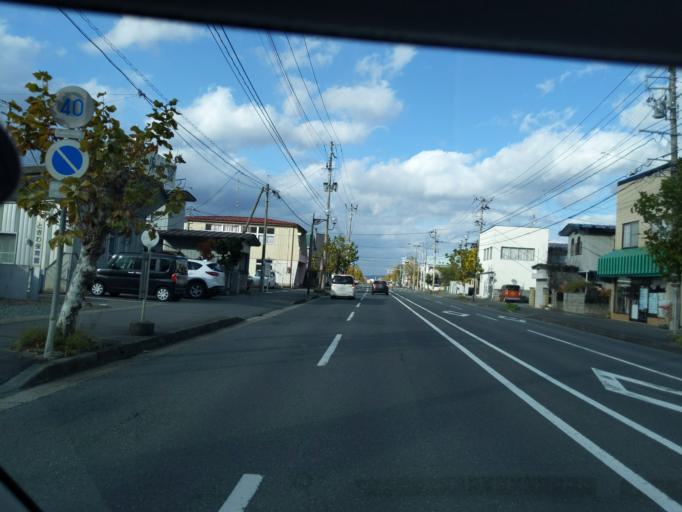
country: JP
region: Iwate
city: Mizusawa
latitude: 39.1375
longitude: 141.1552
